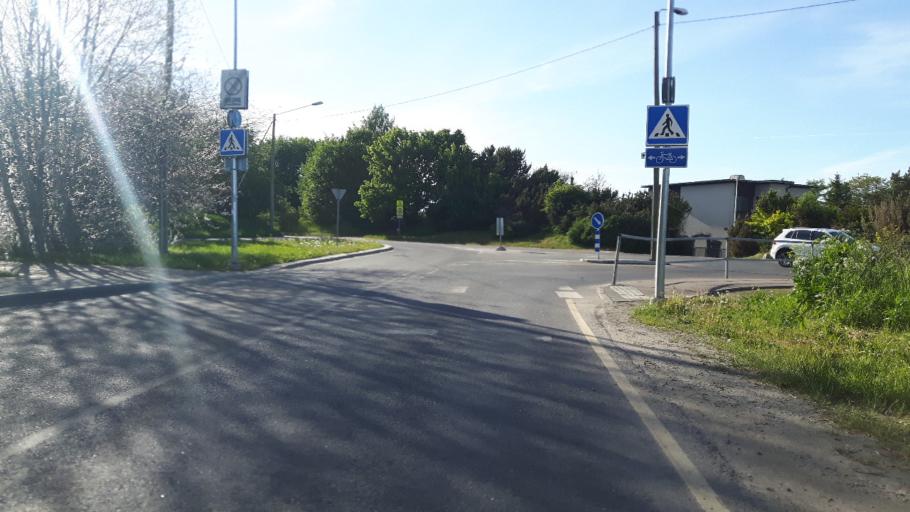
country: EE
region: Harju
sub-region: Tallinna linn
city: Kose
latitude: 59.4546
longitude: 24.8842
